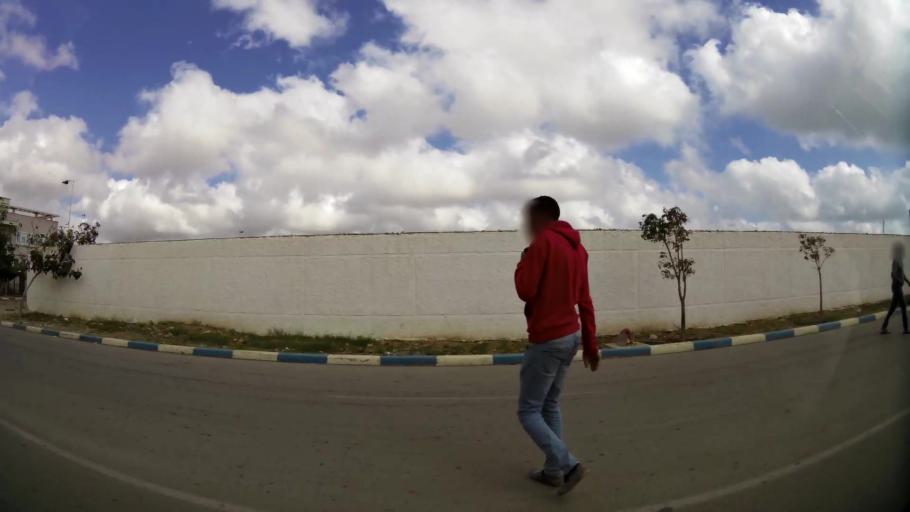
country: MA
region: Oriental
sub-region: Nador
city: Nador
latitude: 35.1656
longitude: -2.9170
